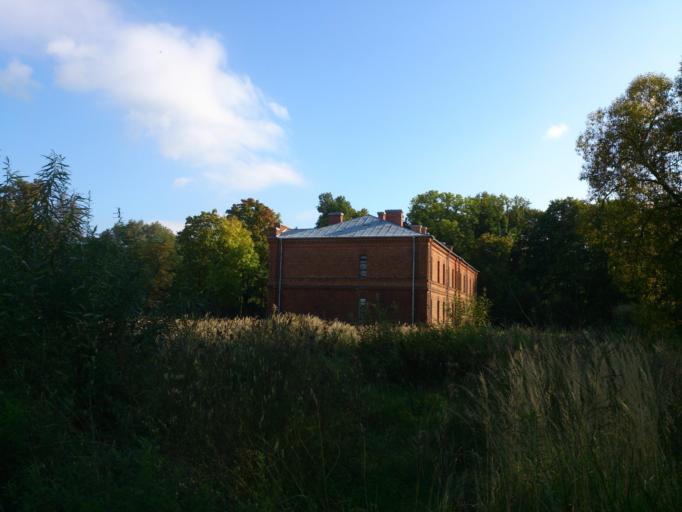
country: LT
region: Kauno apskritis
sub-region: Kaunas
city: Aleksotas
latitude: 54.8748
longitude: 23.9124
